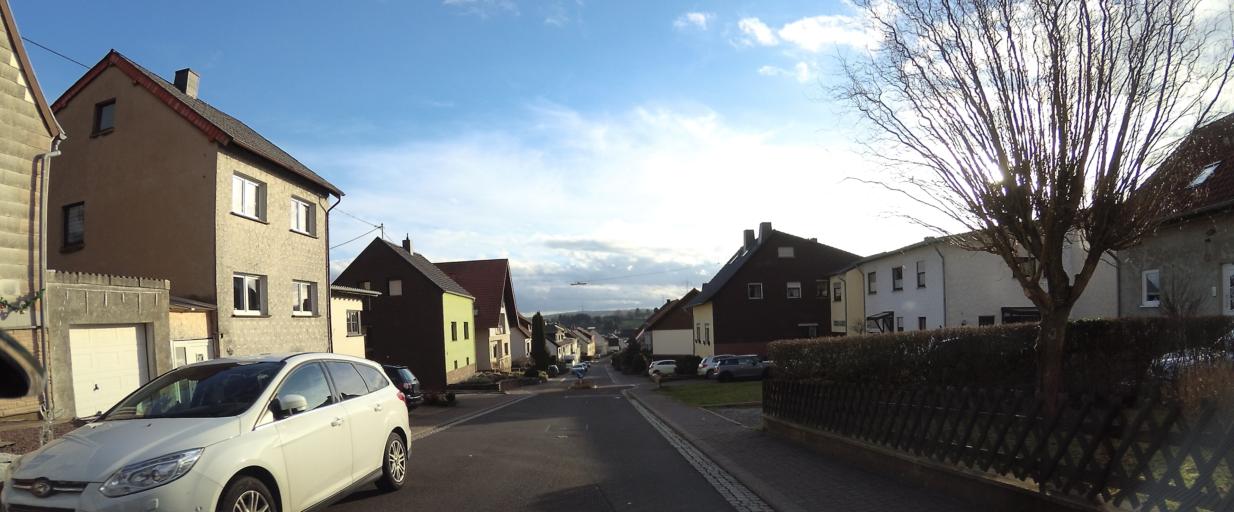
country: DE
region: Saarland
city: Illingen
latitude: 49.3913
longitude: 7.0675
